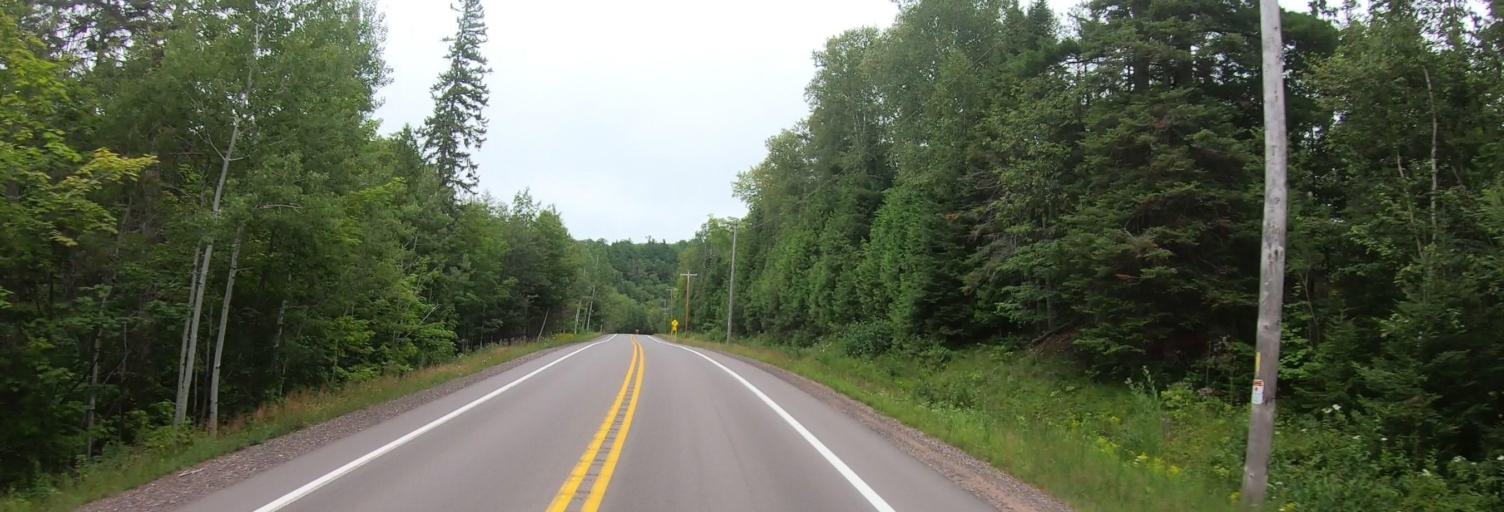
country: US
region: Michigan
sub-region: Keweenaw County
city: Eagle River
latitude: 47.3961
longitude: -88.2825
